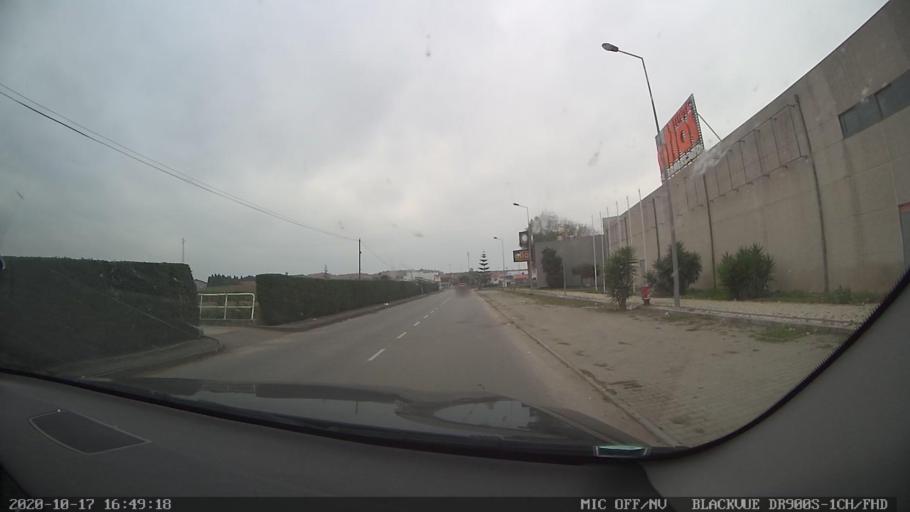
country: PT
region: Braga
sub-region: Esposende
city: Esposende
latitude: 41.5297
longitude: -8.7750
